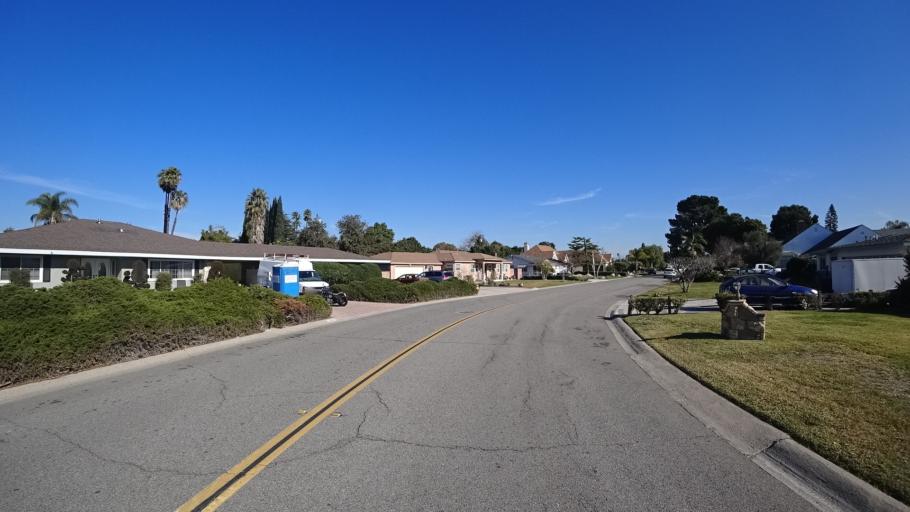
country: US
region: California
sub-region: Orange County
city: Garden Grove
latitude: 33.7877
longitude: -117.9362
